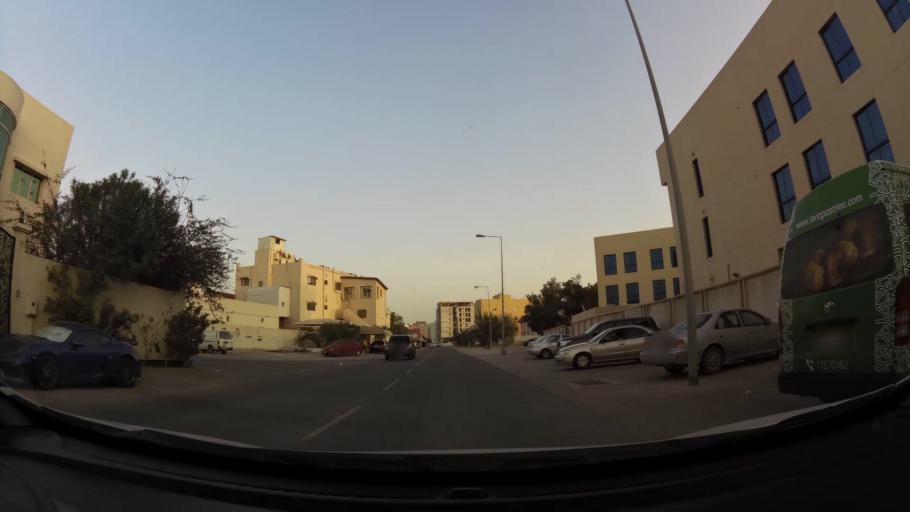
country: BH
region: Northern
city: Madinat `Isa
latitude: 26.1940
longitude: 50.4801
